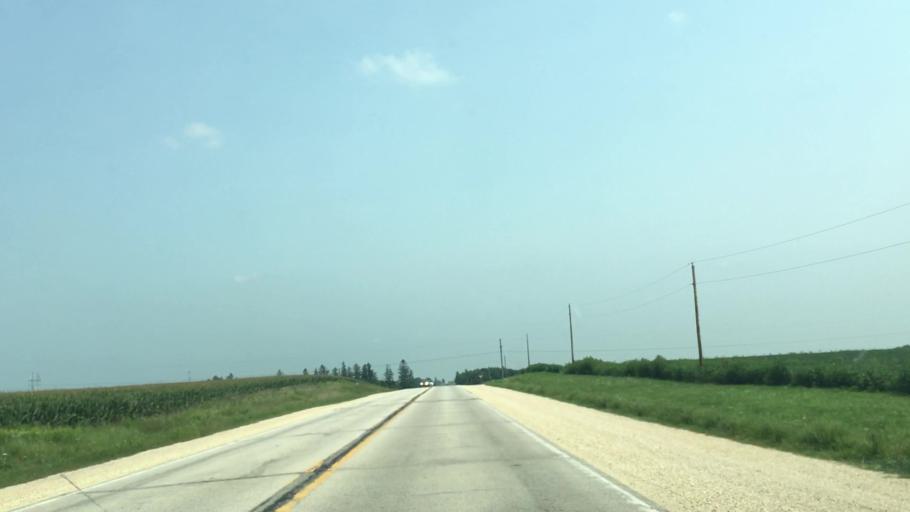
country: US
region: Iowa
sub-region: Fayette County
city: Oelwein
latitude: 42.6798
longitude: -91.8582
